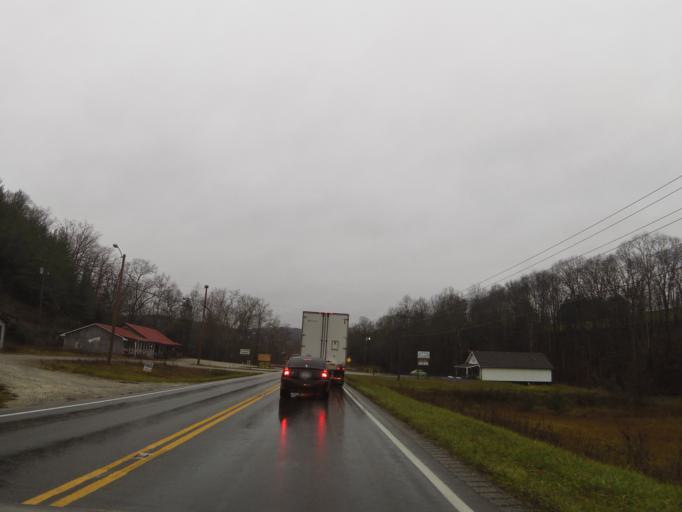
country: US
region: Kentucky
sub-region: Rockcastle County
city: Mount Vernon
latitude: 37.3925
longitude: -84.3332
